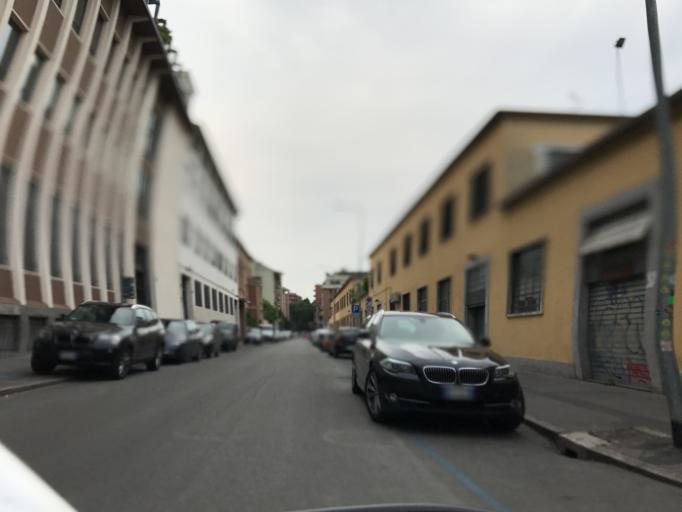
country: IT
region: Lombardy
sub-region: Citta metropolitana di Milano
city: Chiaravalle
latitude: 45.4467
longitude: 9.2215
